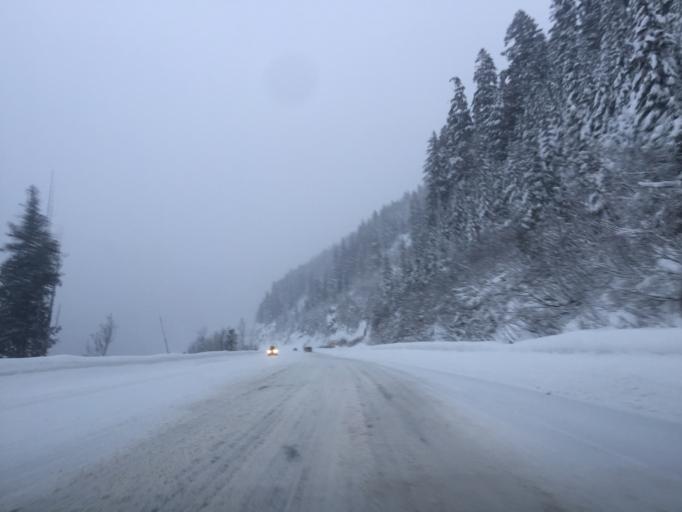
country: US
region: Washington
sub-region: Chelan County
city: Leavenworth
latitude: 47.7367
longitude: -121.1292
